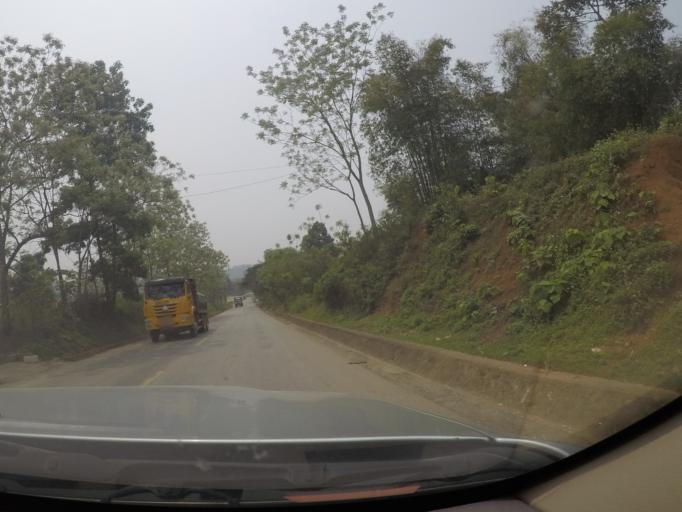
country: VN
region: Thanh Hoa
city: Thi Tran Thuong Xuan
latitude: 19.9697
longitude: 105.4005
